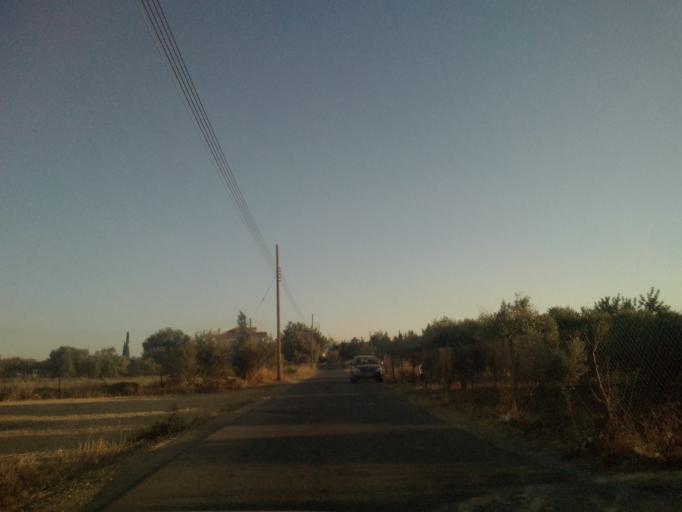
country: CY
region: Limassol
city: Ypsonas
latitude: 34.6788
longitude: 32.9614
